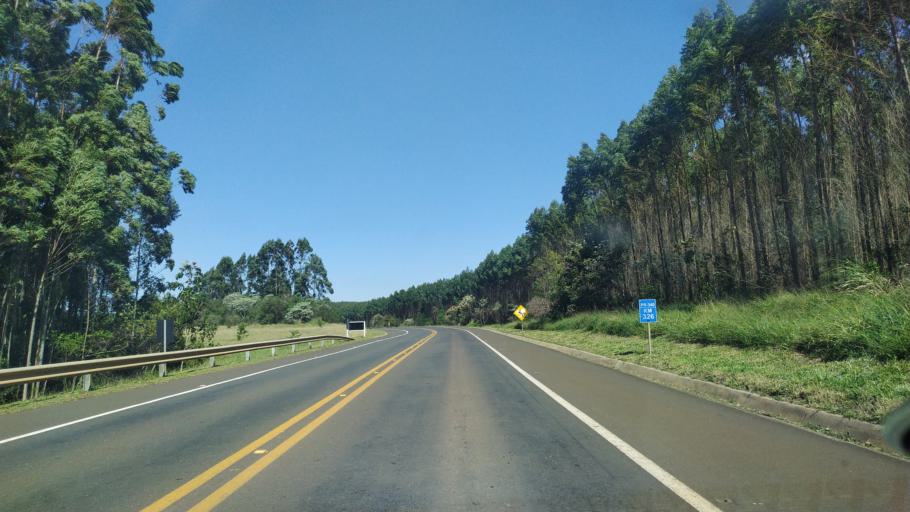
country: BR
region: Parana
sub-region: Ortigueira
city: Ortigueira
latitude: -24.2490
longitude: -50.7769
